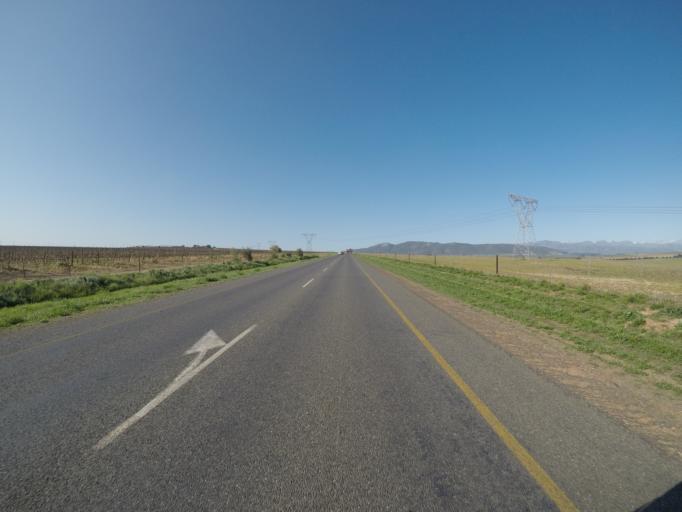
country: ZA
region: Western Cape
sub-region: City of Cape Town
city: Kraaifontein
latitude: -33.7547
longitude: 18.8180
